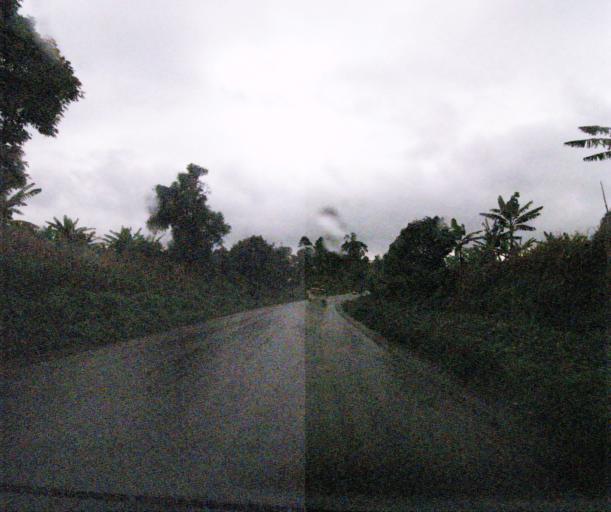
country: CM
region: West
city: Bansoa
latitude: 5.4928
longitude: 10.2627
